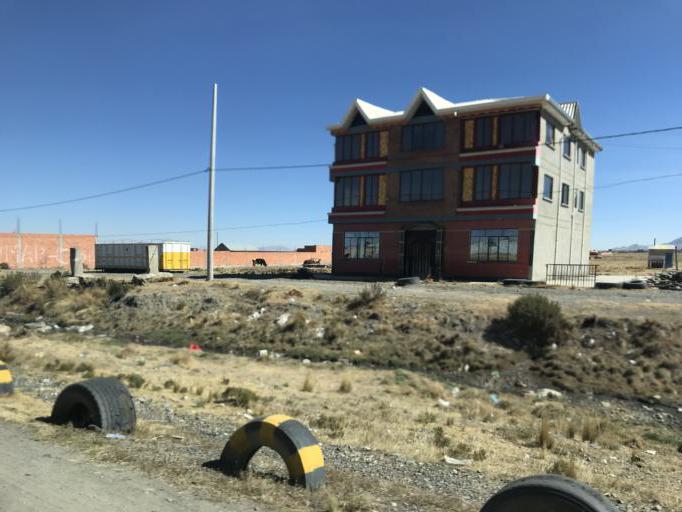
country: BO
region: La Paz
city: La Paz
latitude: -16.5147
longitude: -68.2799
